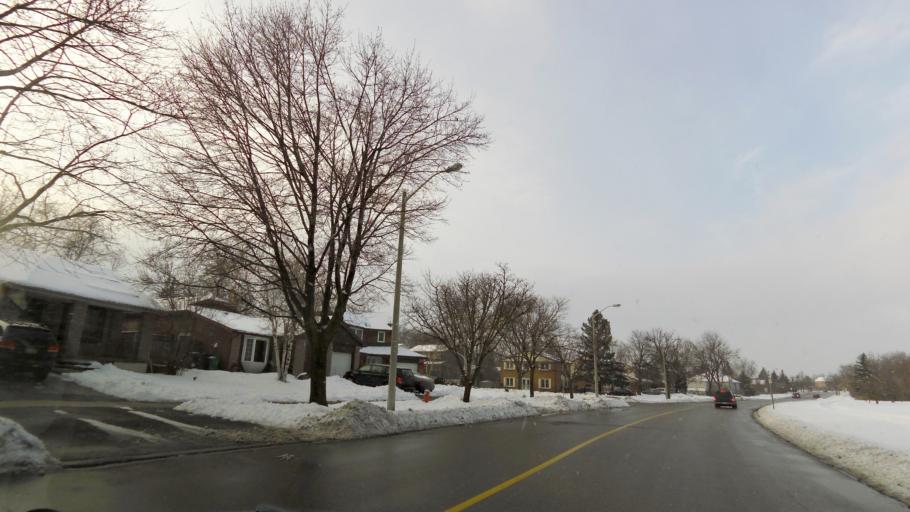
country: CA
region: Ontario
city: Brampton
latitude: 43.7109
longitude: -79.7385
